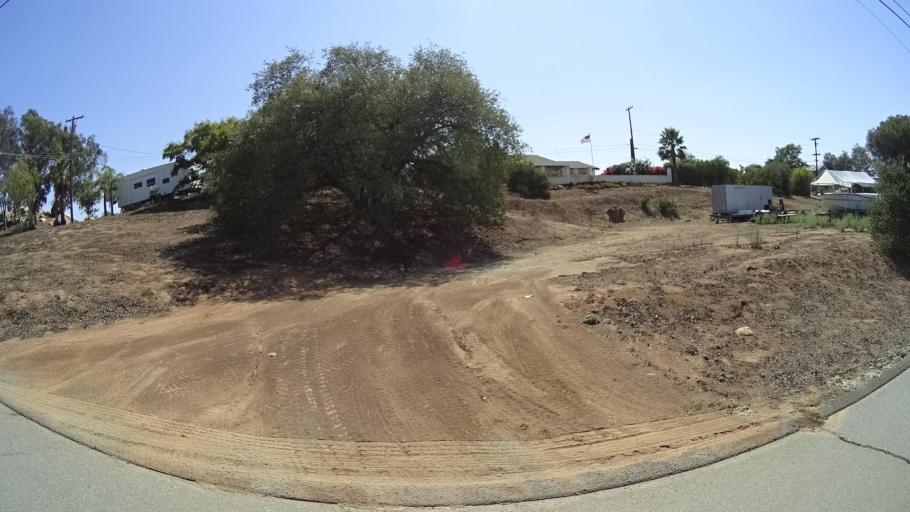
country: US
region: California
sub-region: San Diego County
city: Harbison Canyon
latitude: 32.8216
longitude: -116.8487
